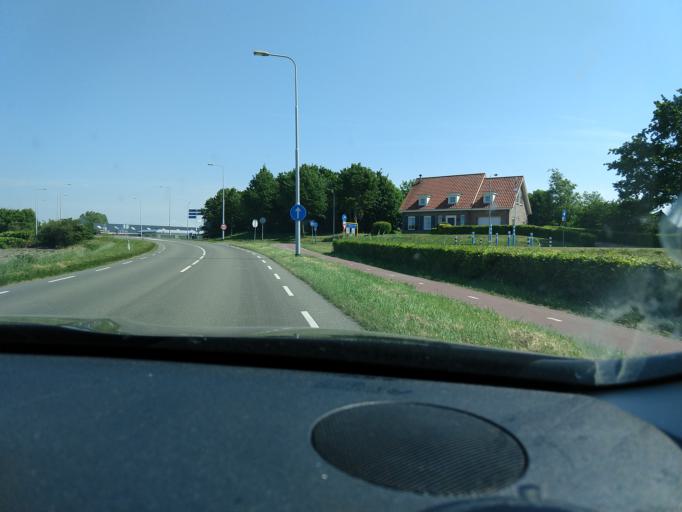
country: NL
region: Zeeland
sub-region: Gemeente Reimerswaal
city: Yerseke
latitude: 51.5493
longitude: 4.0841
